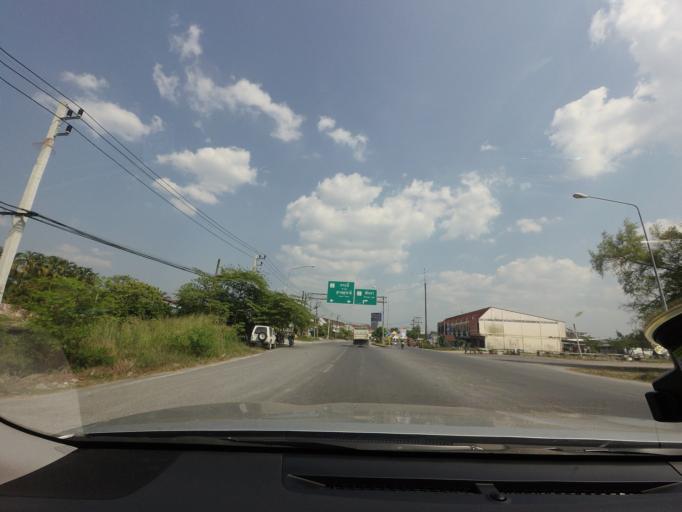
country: TH
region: Phangnga
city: Thap Put
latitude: 8.5215
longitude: 98.6343
